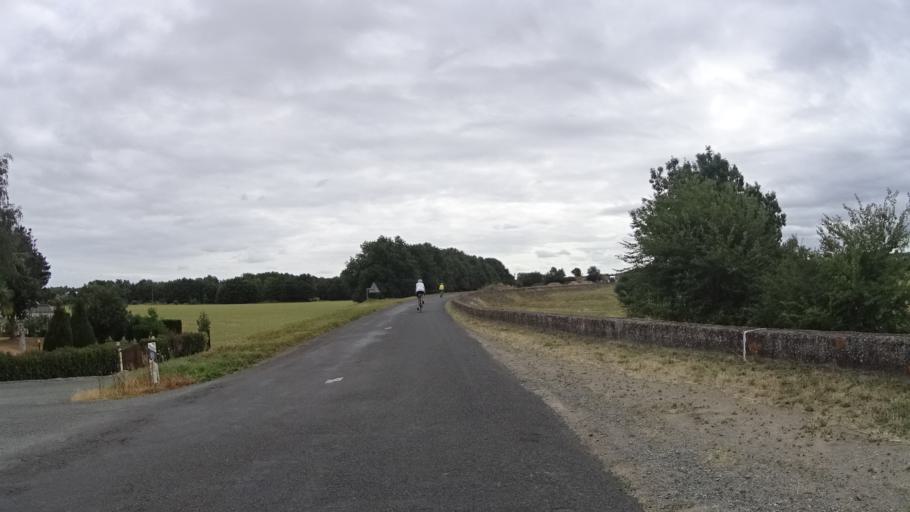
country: FR
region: Pays de la Loire
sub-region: Departement de Maine-et-Loire
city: La Possonniere
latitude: 47.3644
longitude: -0.7245
